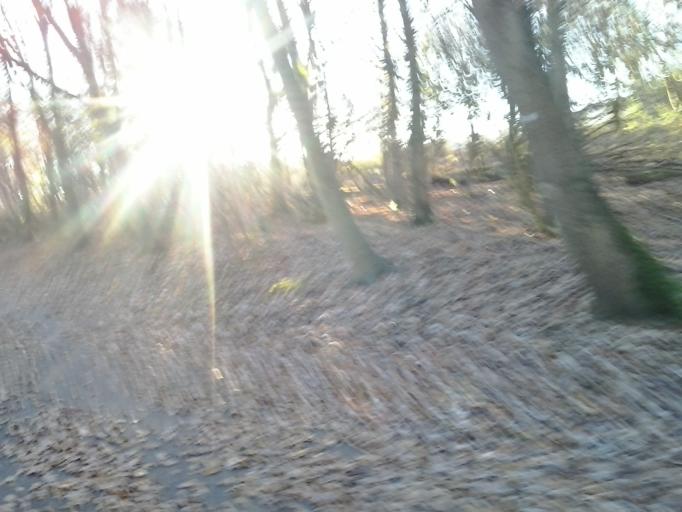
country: NL
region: South Holland
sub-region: Gemeente Lansingerland
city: Bergschenhoek
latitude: 51.9710
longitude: 4.5274
